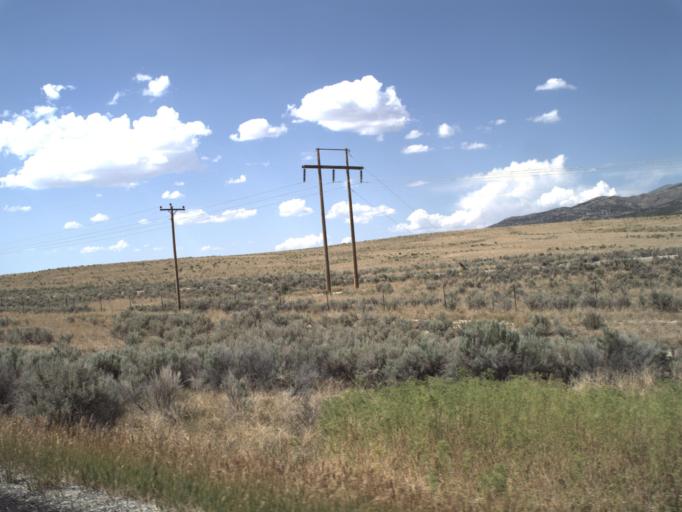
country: US
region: Idaho
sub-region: Minidoka County
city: Rupert
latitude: 41.9852
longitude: -113.1751
